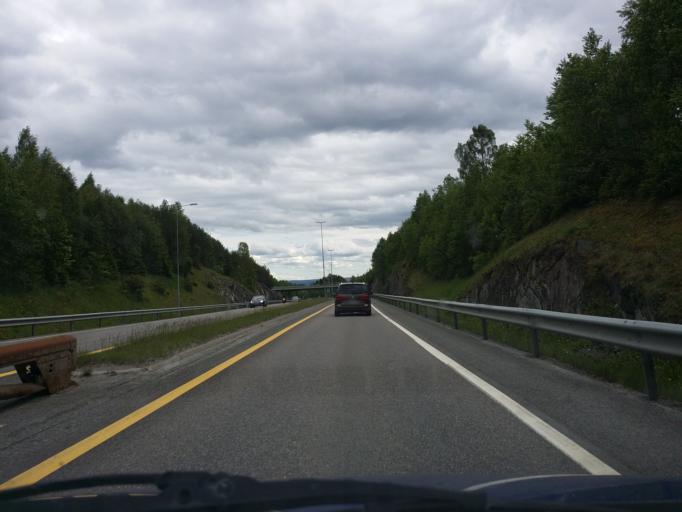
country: NO
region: Hedmark
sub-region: Hamar
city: Hamar
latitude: 60.8461
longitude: 11.0322
